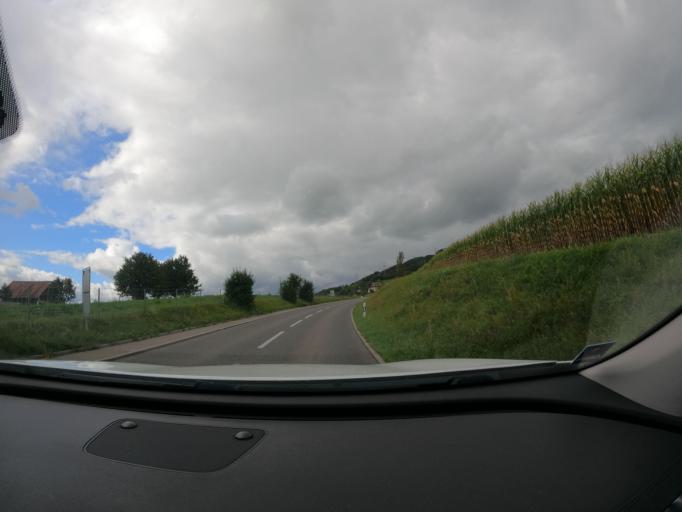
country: CH
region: Lucerne
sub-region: Sursee District
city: Bueron
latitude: 47.2170
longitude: 8.0994
